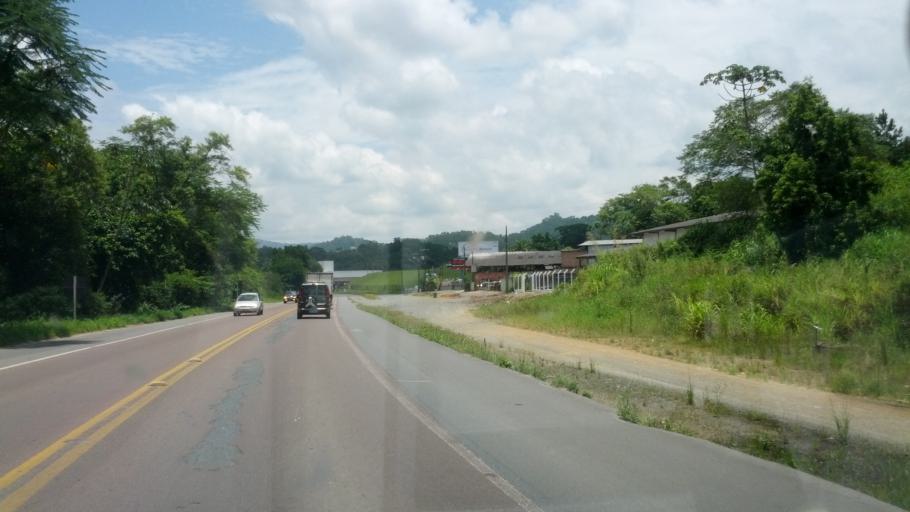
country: BR
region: Santa Catarina
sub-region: Blumenau
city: Blumenau
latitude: -26.8669
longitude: -49.1017
